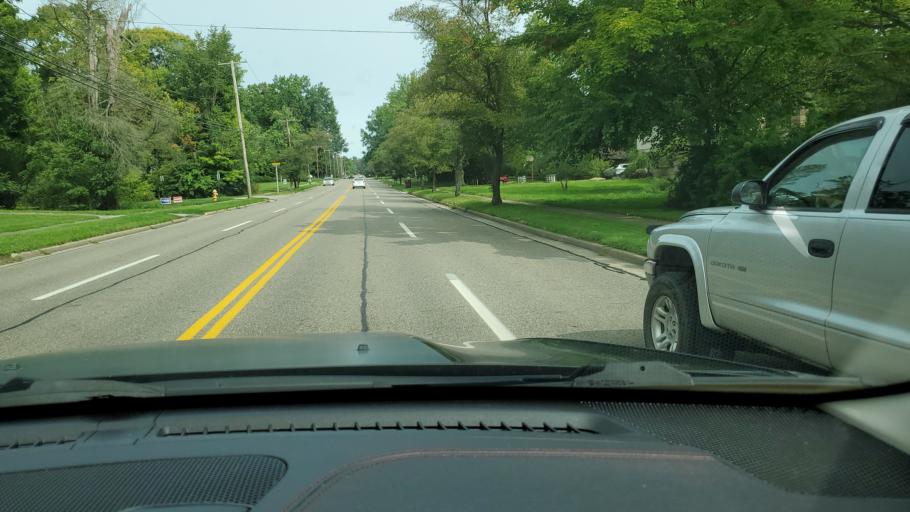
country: US
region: Ohio
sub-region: Mahoning County
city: Boardman
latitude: 41.0378
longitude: -80.6723
